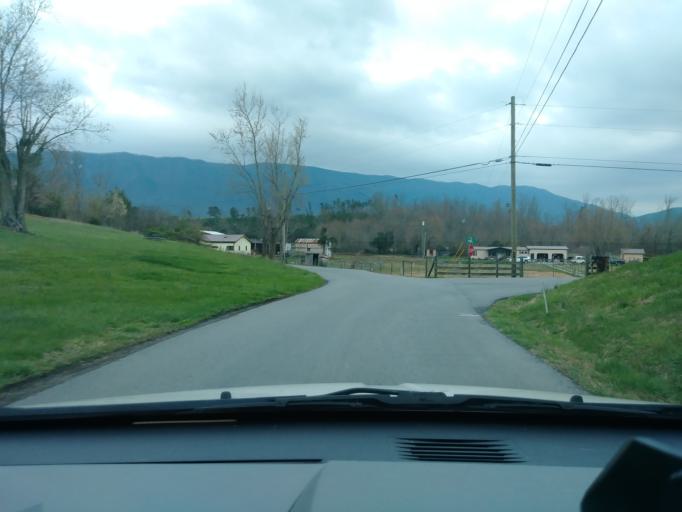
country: US
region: Tennessee
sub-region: Greene County
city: Tusculum
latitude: 36.0873
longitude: -82.7458
